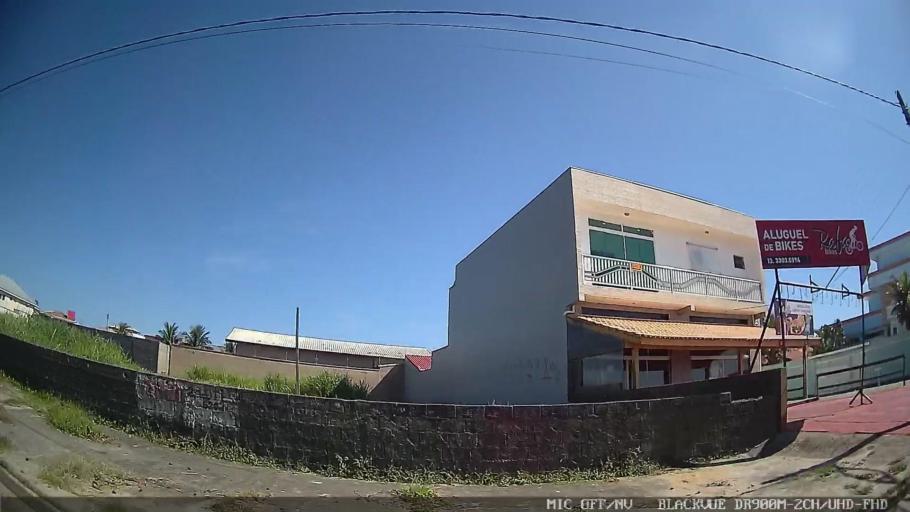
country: BR
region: Sao Paulo
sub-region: Peruibe
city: Peruibe
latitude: -24.2838
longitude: -46.9471
